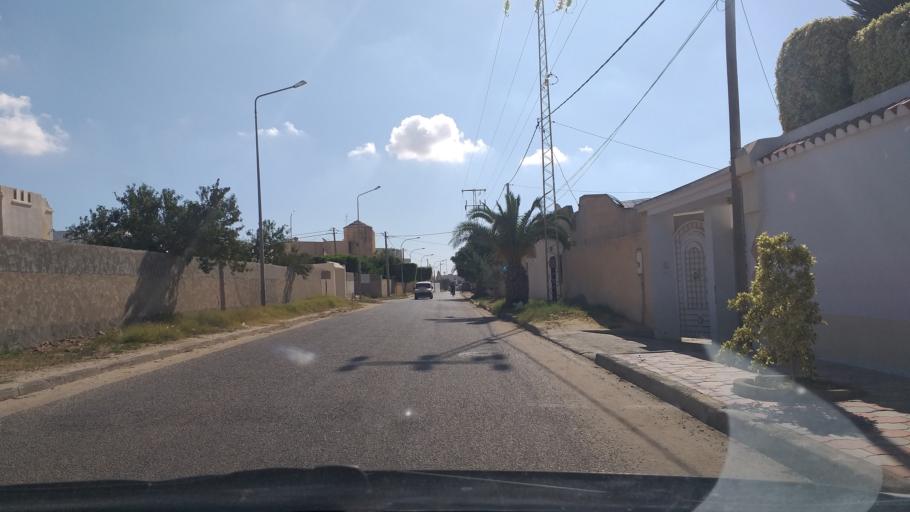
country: TN
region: Safaqis
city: Al Qarmadah
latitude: 34.8041
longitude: 10.7696
